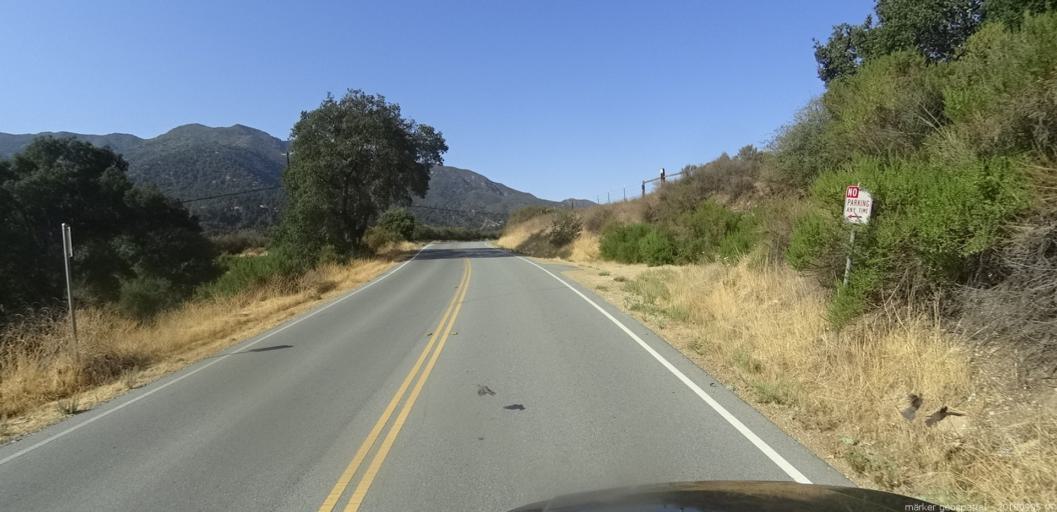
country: US
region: California
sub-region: Monterey County
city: Greenfield
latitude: 36.2357
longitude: -121.4518
